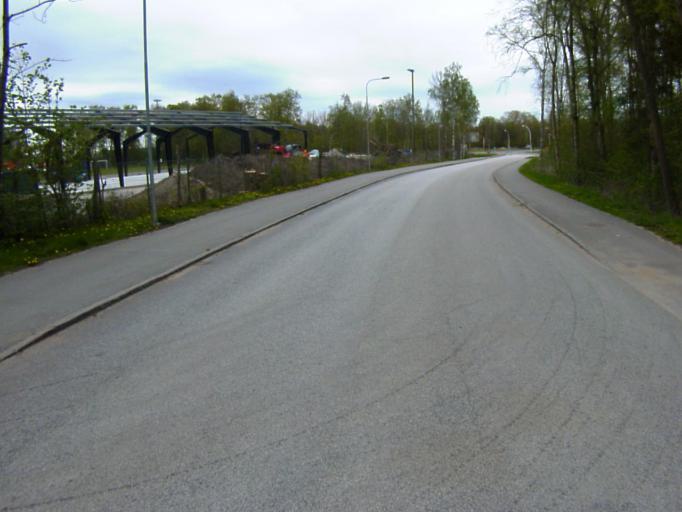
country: SE
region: Skane
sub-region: Kristianstads Kommun
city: Kristianstad
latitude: 56.0231
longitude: 14.1680
